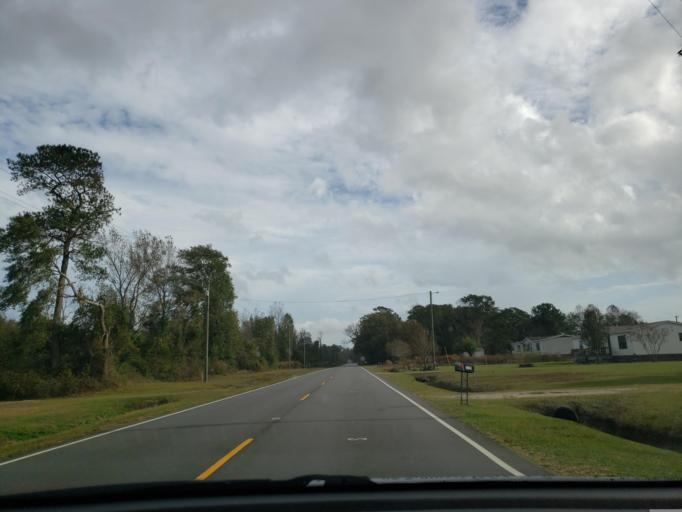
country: US
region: North Carolina
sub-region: Duplin County
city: Beulaville
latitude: 34.8368
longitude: -77.8590
